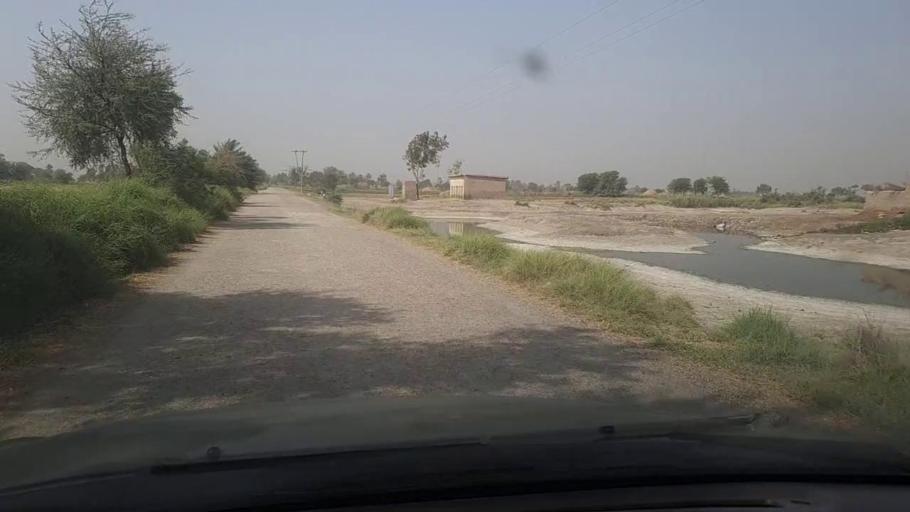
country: PK
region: Sindh
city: Garhi Yasin
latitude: 27.8766
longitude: 68.5641
